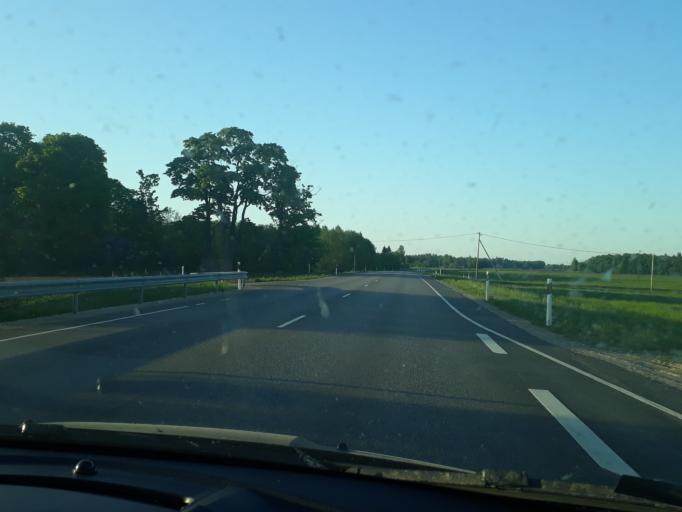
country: EE
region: Paernumaa
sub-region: Tootsi vald
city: Tootsi
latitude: 58.5659
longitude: 24.8726
